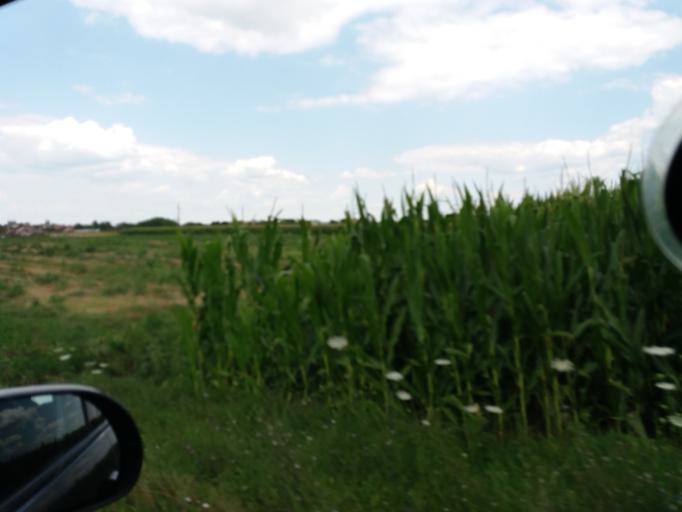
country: RS
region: Autonomna Pokrajina Vojvodina
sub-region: Sremski Okrug
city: Pecinci
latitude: 44.9015
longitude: 19.9573
